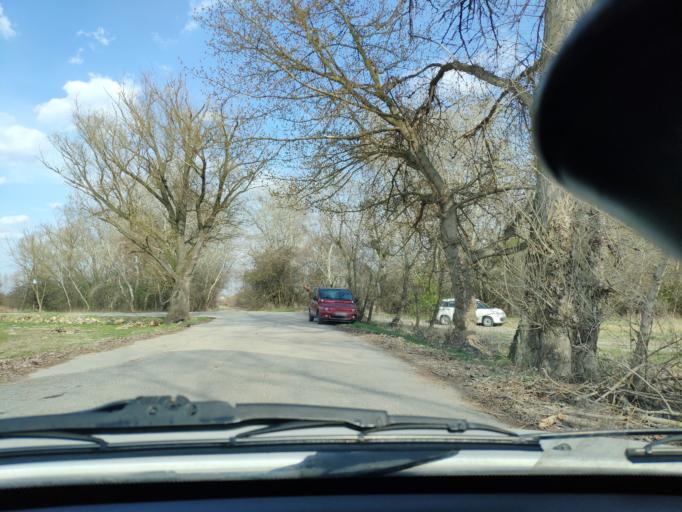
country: HU
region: Fejer
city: Adony
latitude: 47.1133
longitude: 18.8890
